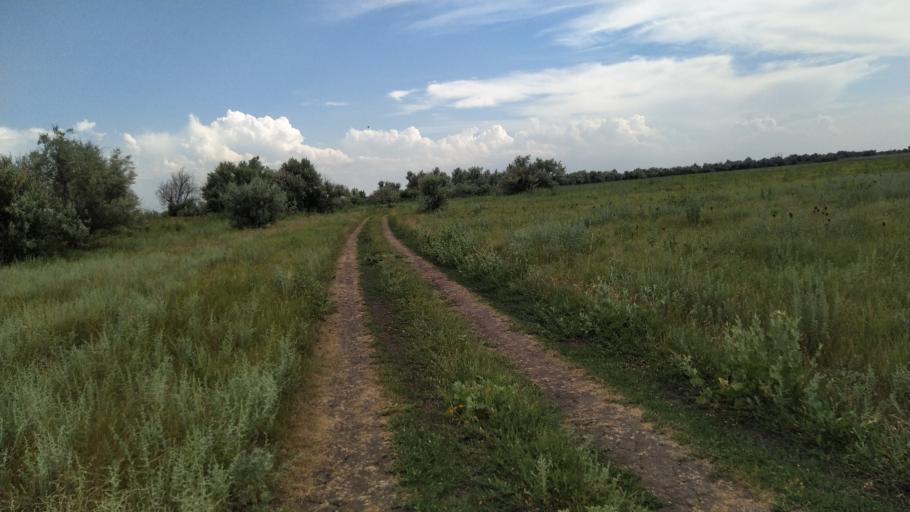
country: RU
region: Rostov
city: Kuleshovka
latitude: 47.1282
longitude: 39.6295
